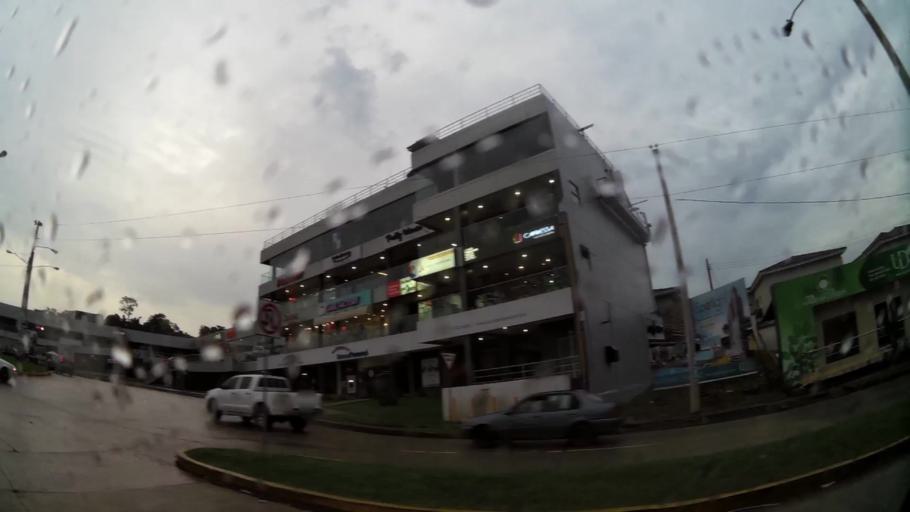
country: PA
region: Panama
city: Panama
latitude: 9.0329
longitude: -79.5332
